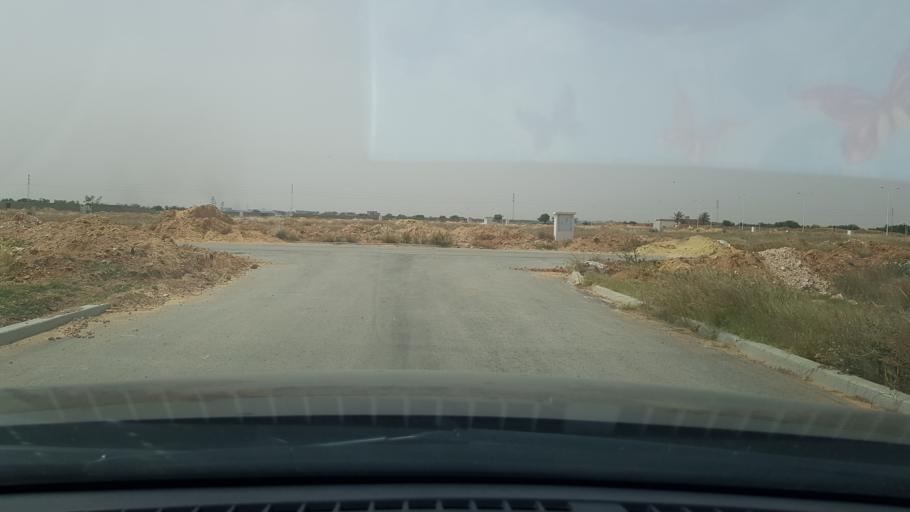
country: TN
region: Safaqis
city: Al Qarmadah
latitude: 34.8283
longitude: 10.7433
